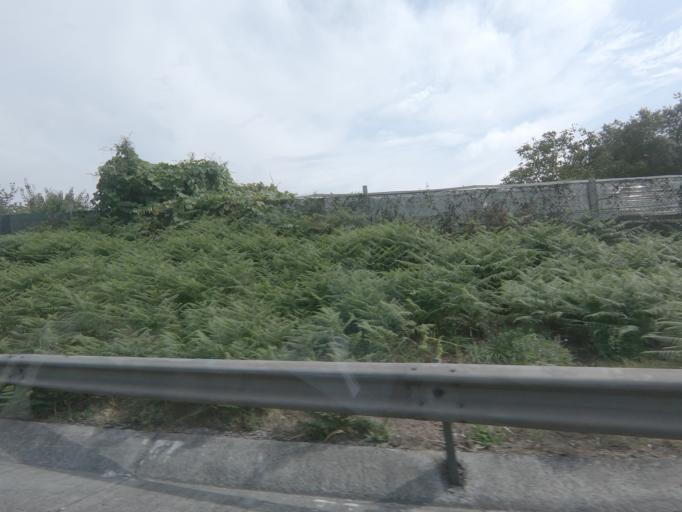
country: PT
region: Leiria
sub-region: Leiria
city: Leiria
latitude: 39.7612
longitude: -8.8013
